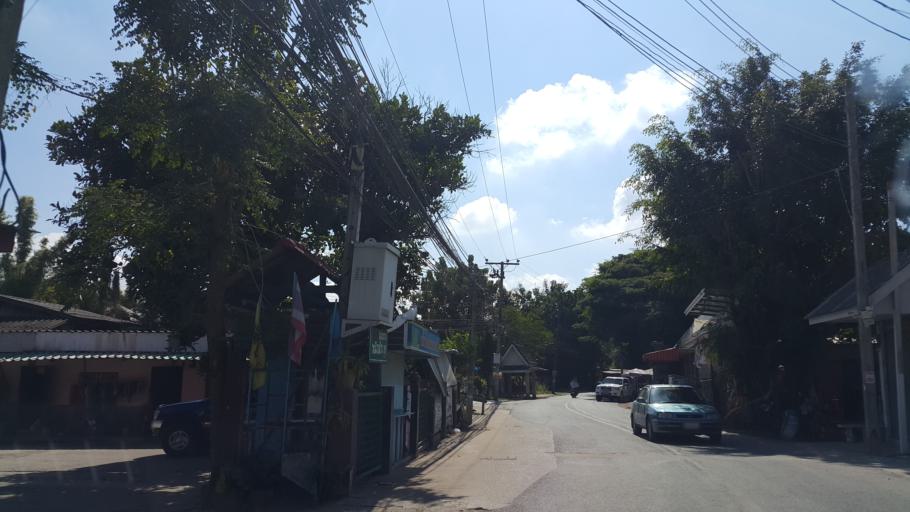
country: TH
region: Chiang Mai
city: San Sai
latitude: 18.8307
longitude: 99.0201
